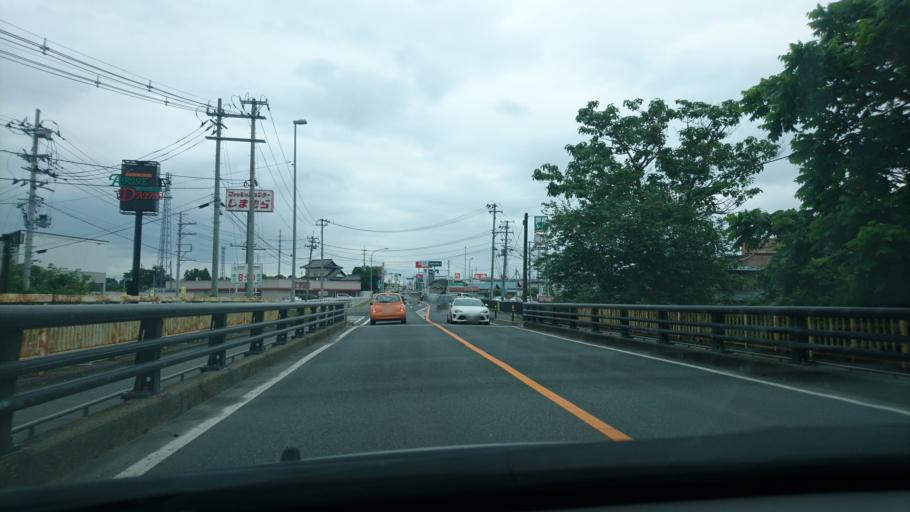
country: JP
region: Miyagi
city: Furukawa
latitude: 38.7409
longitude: 141.0185
